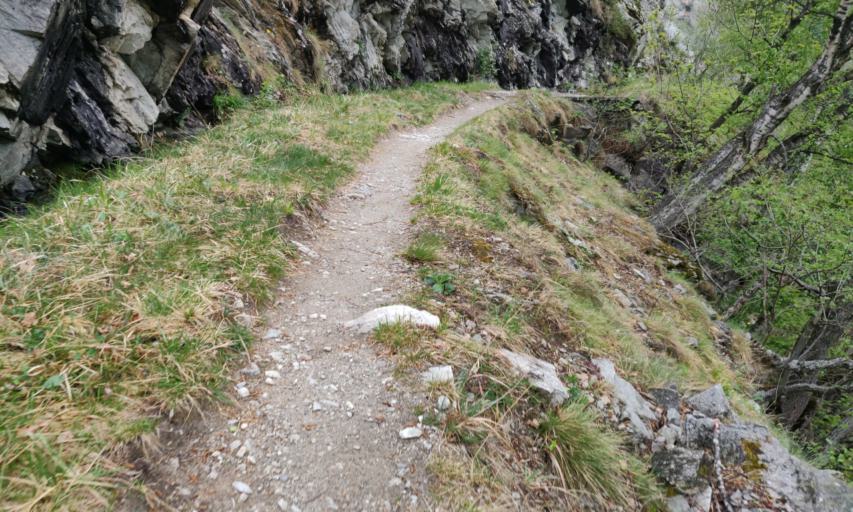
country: CH
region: Valais
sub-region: Visp District
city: Baltschieder
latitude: 46.3185
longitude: 7.8837
